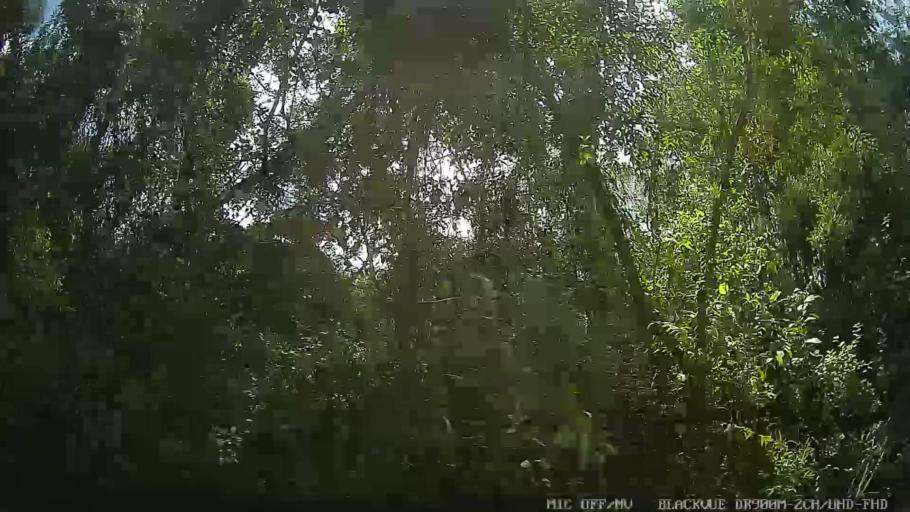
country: BR
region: Sao Paulo
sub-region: Mogi das Cruzes
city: Mogi das Cruzes
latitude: -23.6874
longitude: -46.2186
